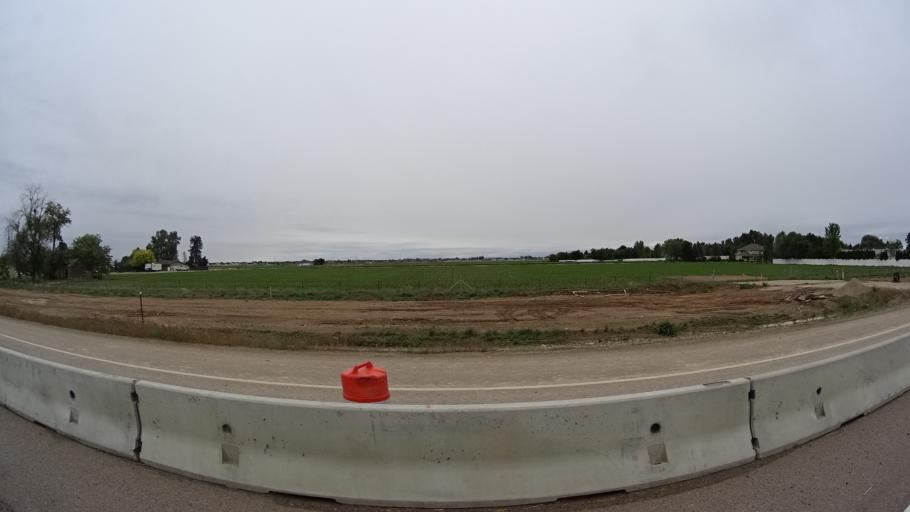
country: US
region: Idaho
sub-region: Ada County
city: Star
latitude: 43.6633
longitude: -116.4650
